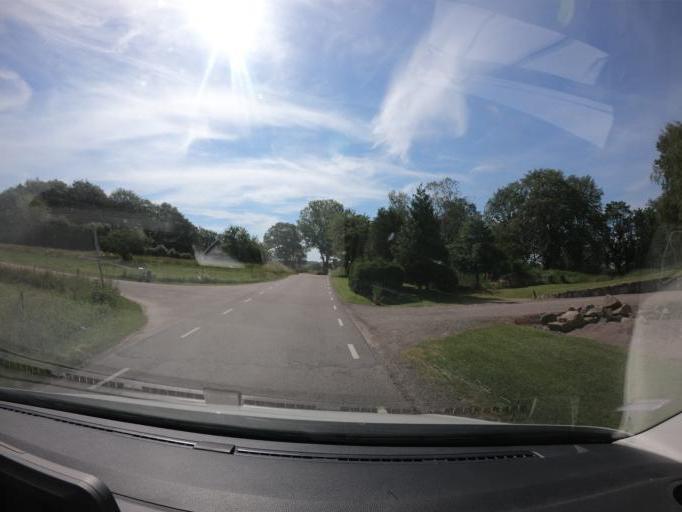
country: SE
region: Skane
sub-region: Bastads Kommun
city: Forslov
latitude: 56.4160
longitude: 12.7767
